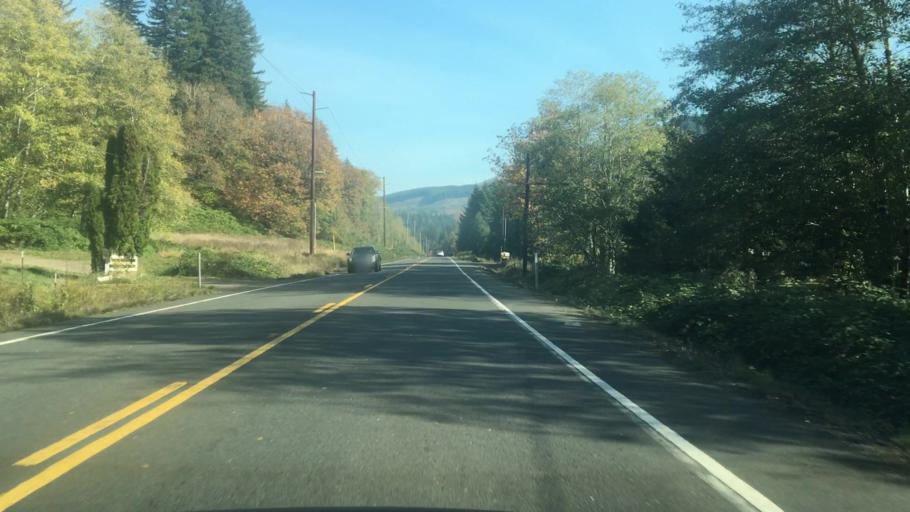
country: US
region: Oregon
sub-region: Lincoln County
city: Rose Lodge
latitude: 45.0218
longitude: -123.8449
